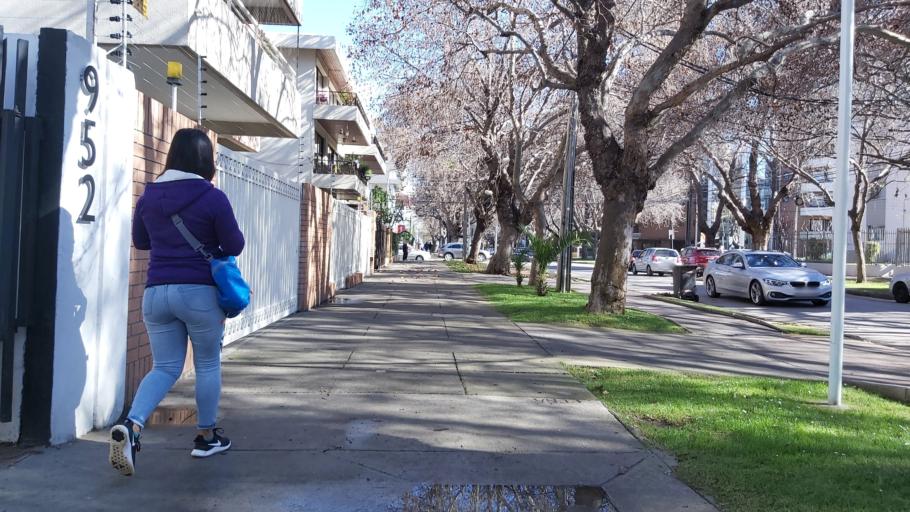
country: CL
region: Valparaiso
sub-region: Provincia de Valparaiso
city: Vina del Mar
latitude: -33.0159
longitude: -71.5468
